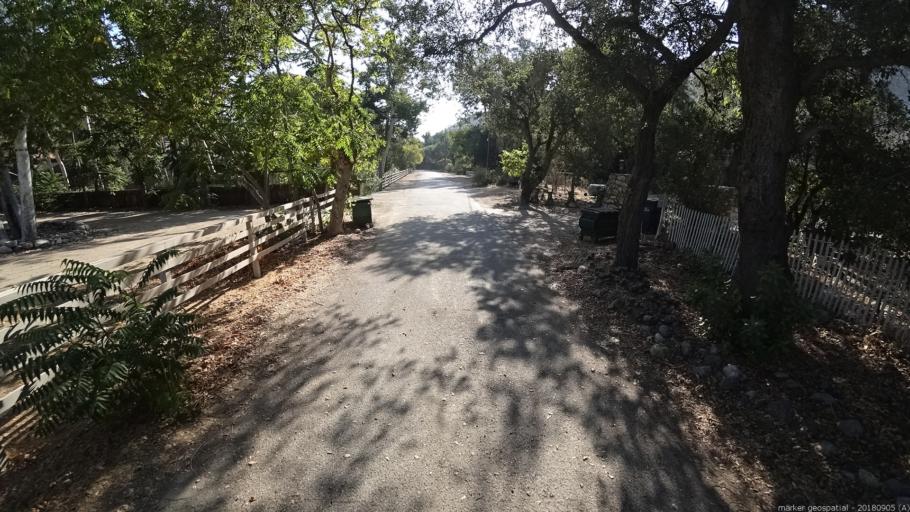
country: US
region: California
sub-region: Monterey County
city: Greenfield
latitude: 36.2637
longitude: -121.3959
